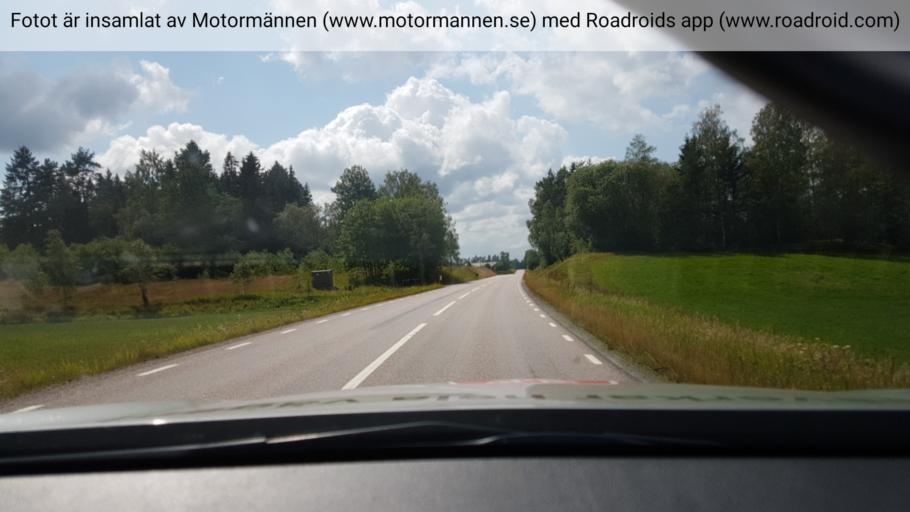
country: SE
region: Vaestra Goetaland
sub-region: Svenljunga Kommun
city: Svenljunga
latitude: 57.4858
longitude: 13.0547
